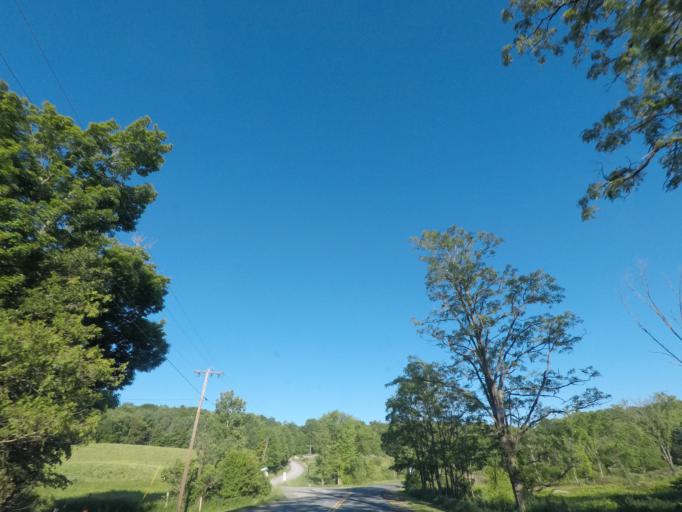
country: US
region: New York
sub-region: Rensselaer County
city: Averill Park
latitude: 42.5766
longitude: -73.5352
